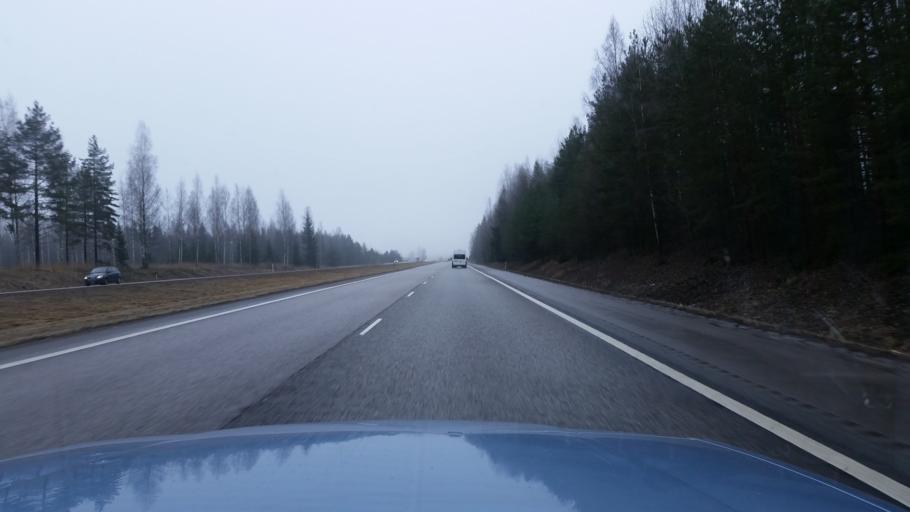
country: FI
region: Uusimaa
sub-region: Helsinki
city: Nurmijaervi
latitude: 60.5077
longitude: 24.8488
